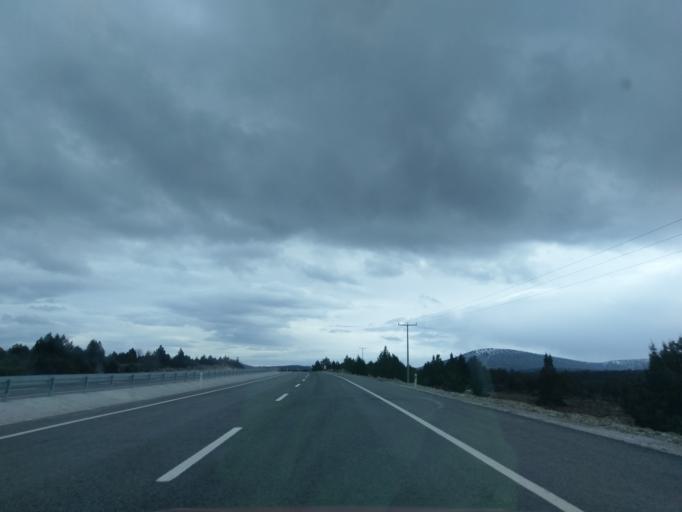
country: TR
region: Kuetahya
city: Cavdarhisar
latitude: 39.2232
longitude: 29.7305
